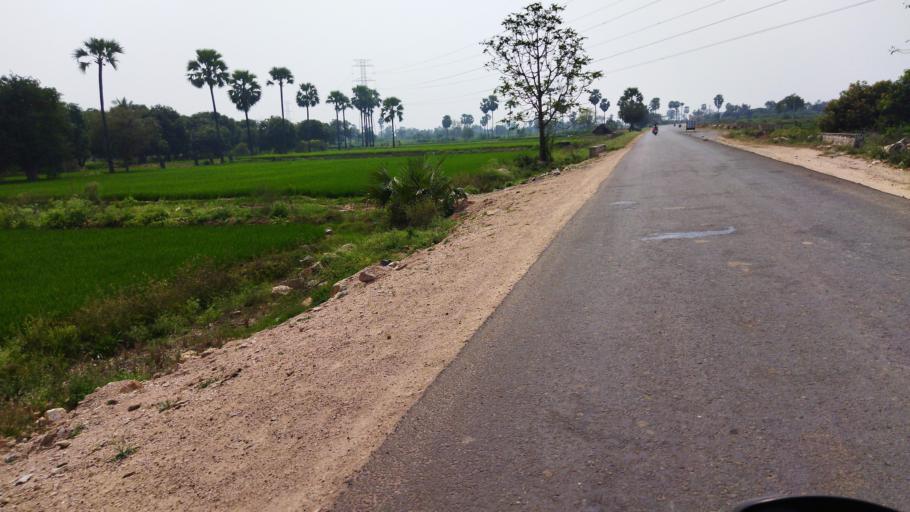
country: IN
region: Telangana
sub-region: Nalgonda
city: Nalgonda
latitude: 17.1154
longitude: 79.3616
